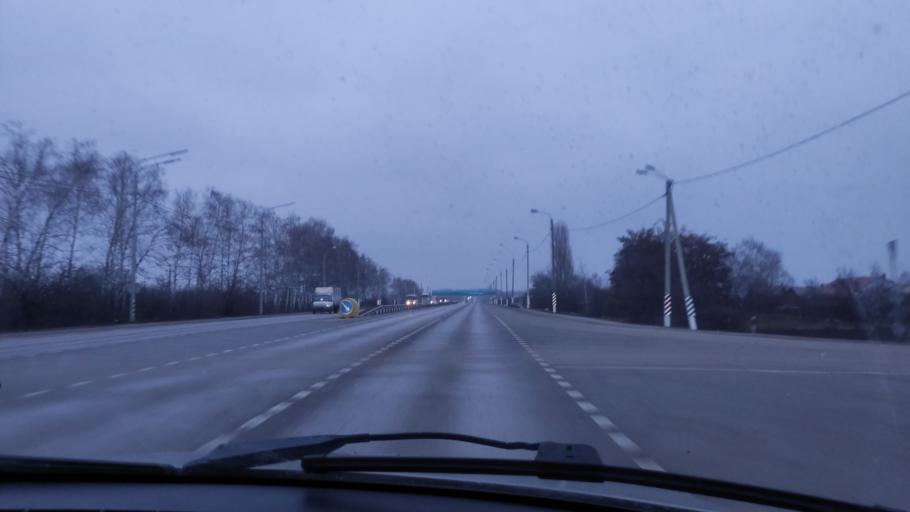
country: RU
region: Tambov
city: Komsomolets
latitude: 52.7307
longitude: 41.3138
